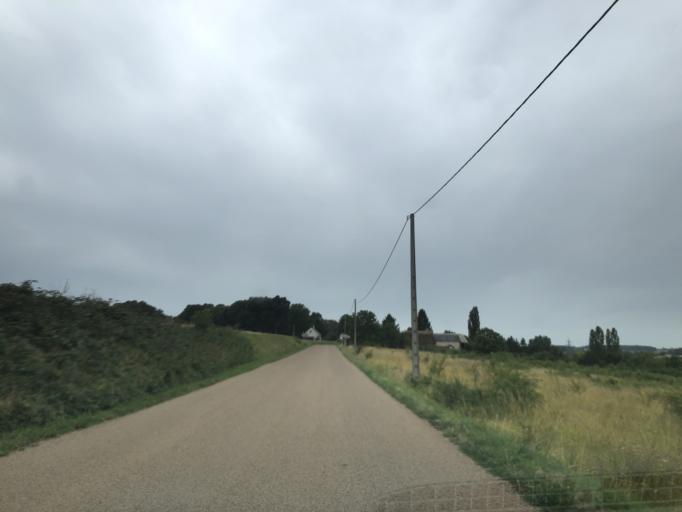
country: FR
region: Bourgogne
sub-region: Departement de l'Yonne
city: Charny
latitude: 47.9464
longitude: 3.1330
